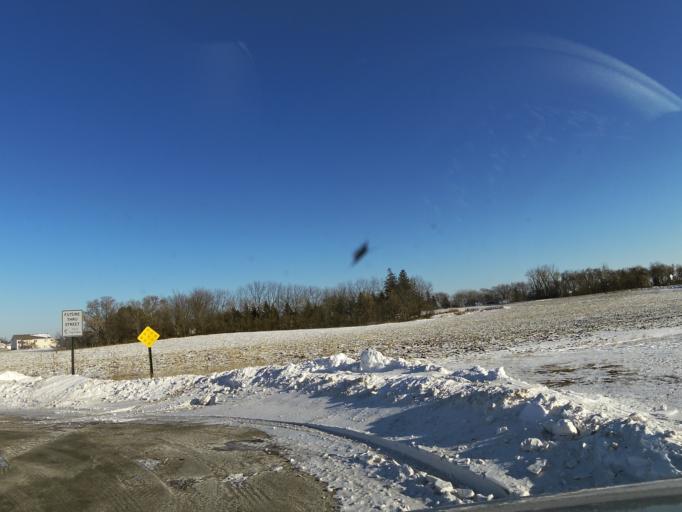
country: US
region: Minnesota
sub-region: Le Sueur County
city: New Prague
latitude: 44.5452
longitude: -93.5952
